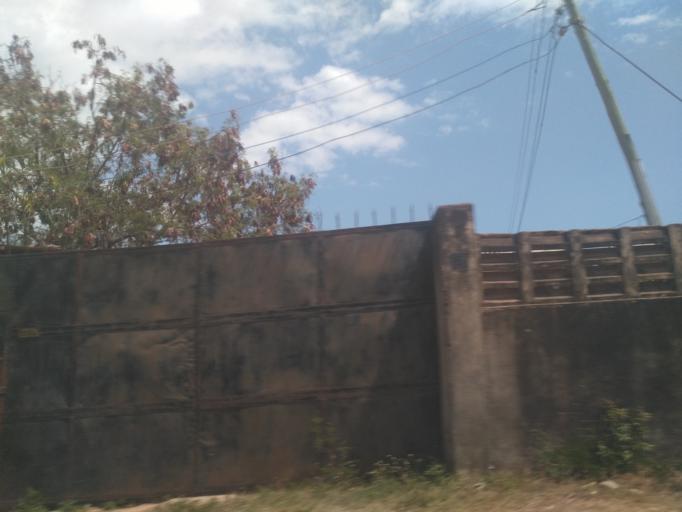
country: TZ
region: Dar es Salaam
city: Magomeni
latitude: -6.7467
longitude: 39.2818
